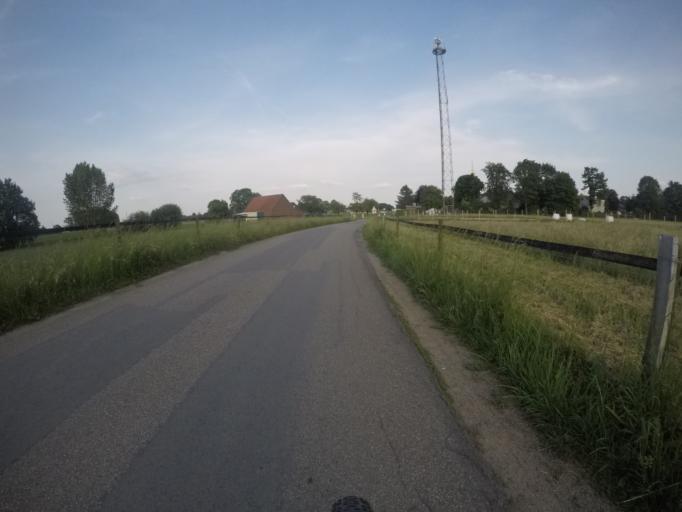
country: DE
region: North Rhine-Westphalia
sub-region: Regierungsbezirk Munster
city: Isselburg
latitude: 51.8206
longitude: 6.4403
